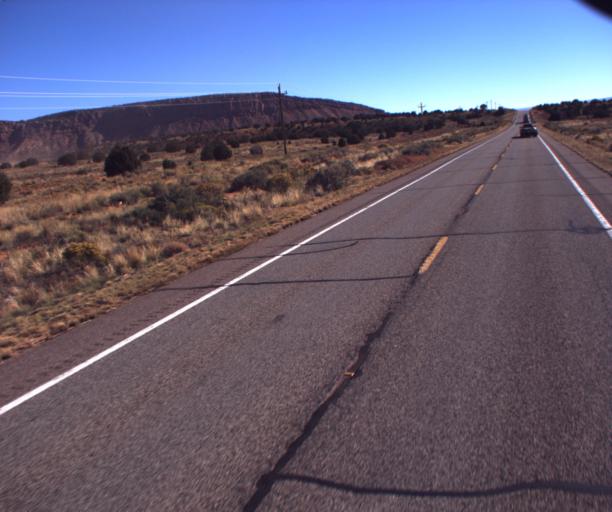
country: US
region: Arizona
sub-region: Mohave County
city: Colorado City
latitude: 36.8581
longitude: -112.7832
